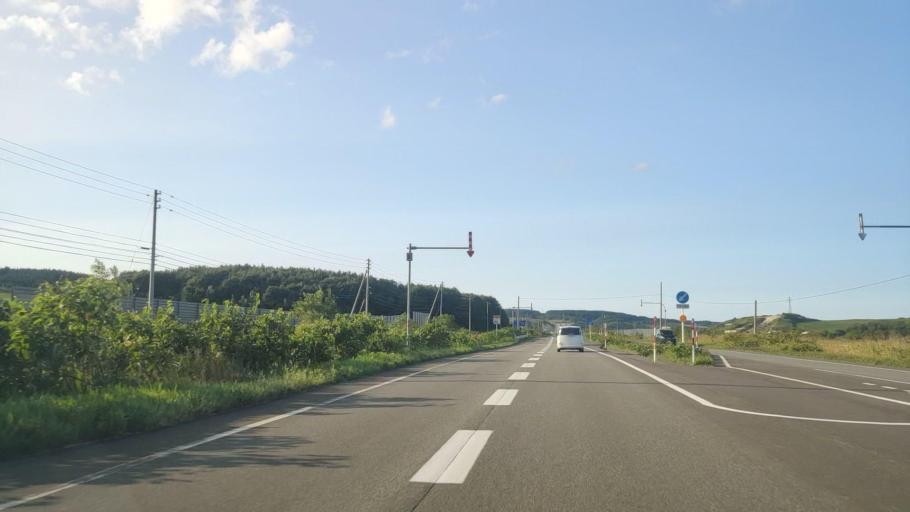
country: JP
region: Hokkaido
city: Wakkanai
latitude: 45.3227
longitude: 141.7194
